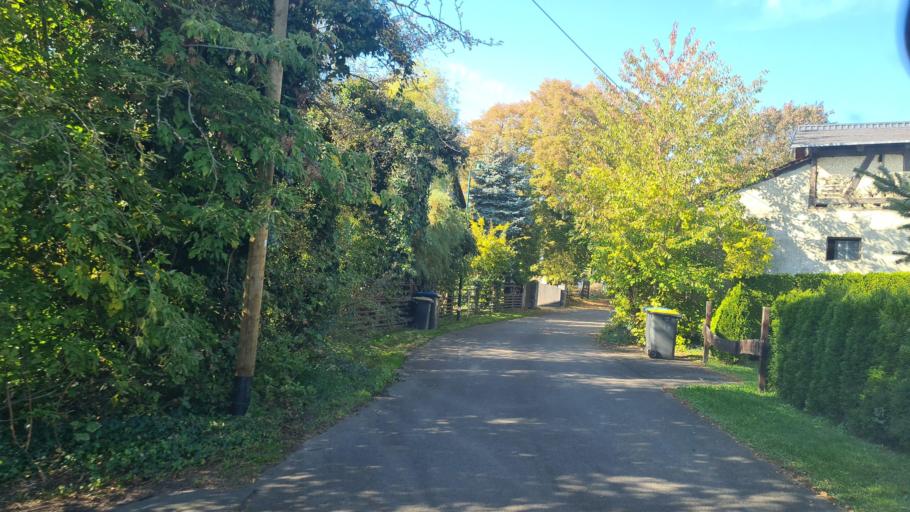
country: DE
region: Saxony
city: Borna
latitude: 51.1509
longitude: 12.4889
